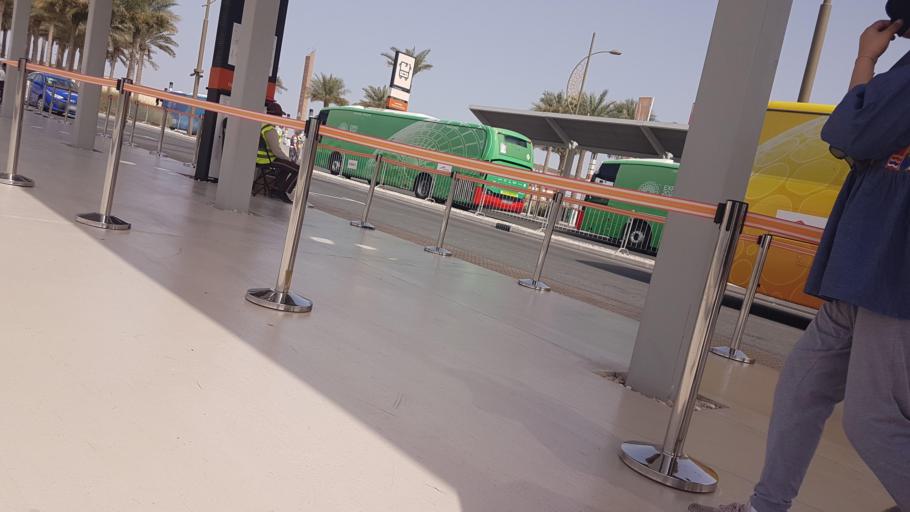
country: AE
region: Dubai
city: Dubai
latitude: 24.9678
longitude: 55.1544
